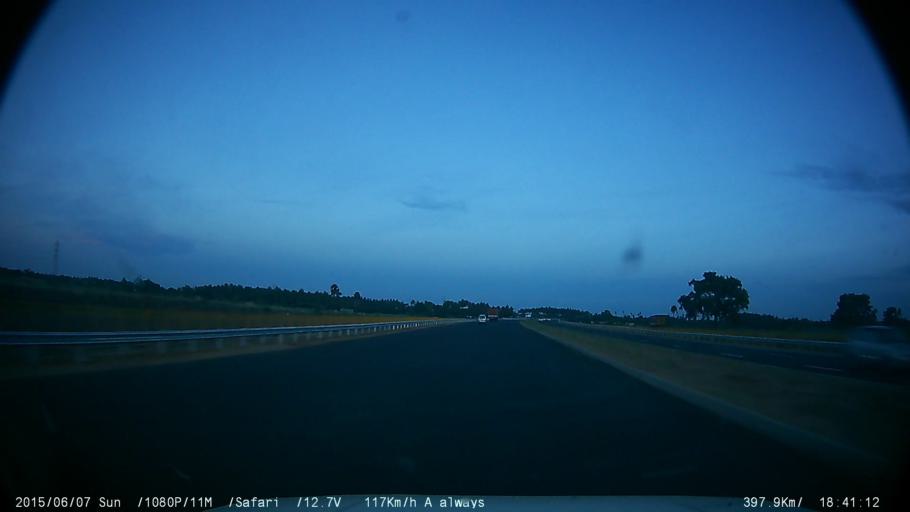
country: IN
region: Tamil Nadu
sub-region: Tiruppur
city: Tiruppur
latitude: 11.2112
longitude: 77.3666
